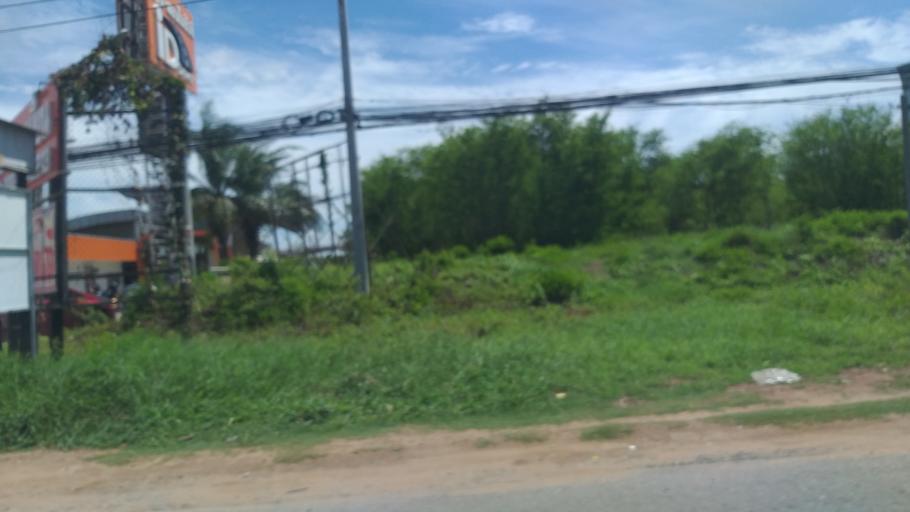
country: TH
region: Khon Kaen
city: Khon Kaen
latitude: 16.4439
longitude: 102.8002
